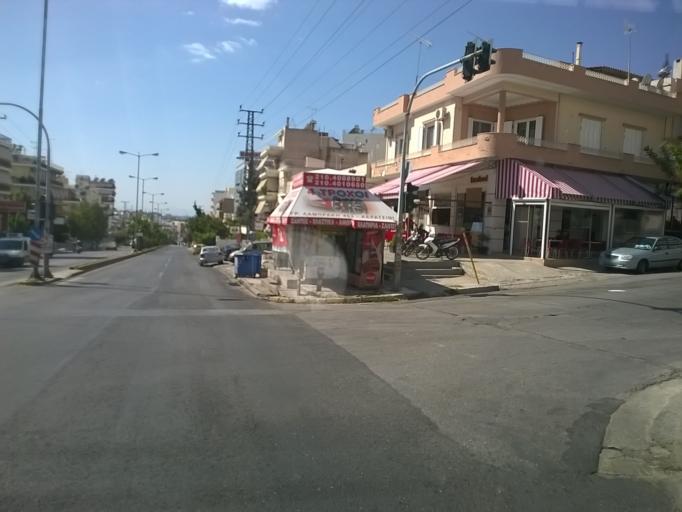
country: GR
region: Attica
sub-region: Nomos Piraios
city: Keratsini
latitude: 37.9682
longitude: 23.6179
